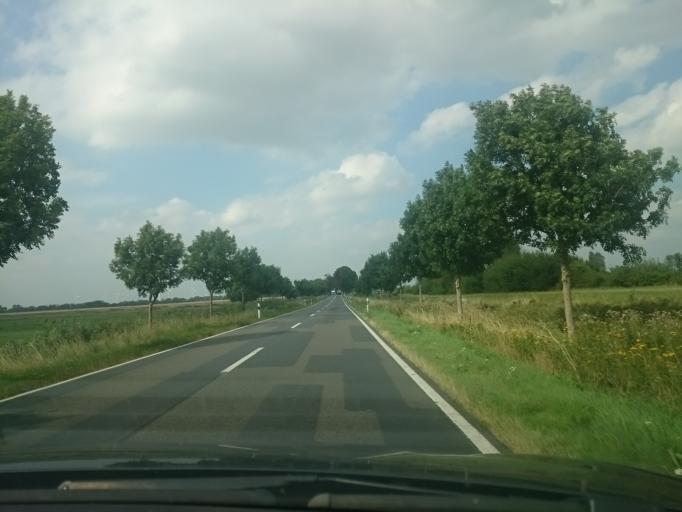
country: DE
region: Mecklenburg-Vorpommern
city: Ducherow
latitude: 53.7436
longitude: 13.7834
